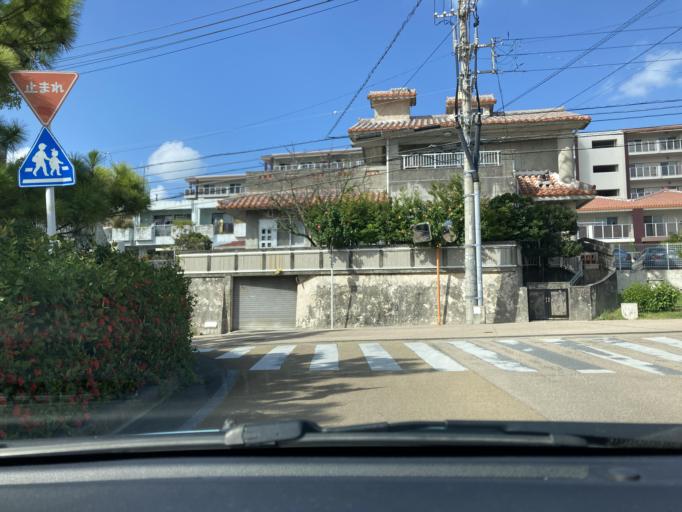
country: JP
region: Okinawa
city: Naha-shi
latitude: 26.2175
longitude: 127.7115
